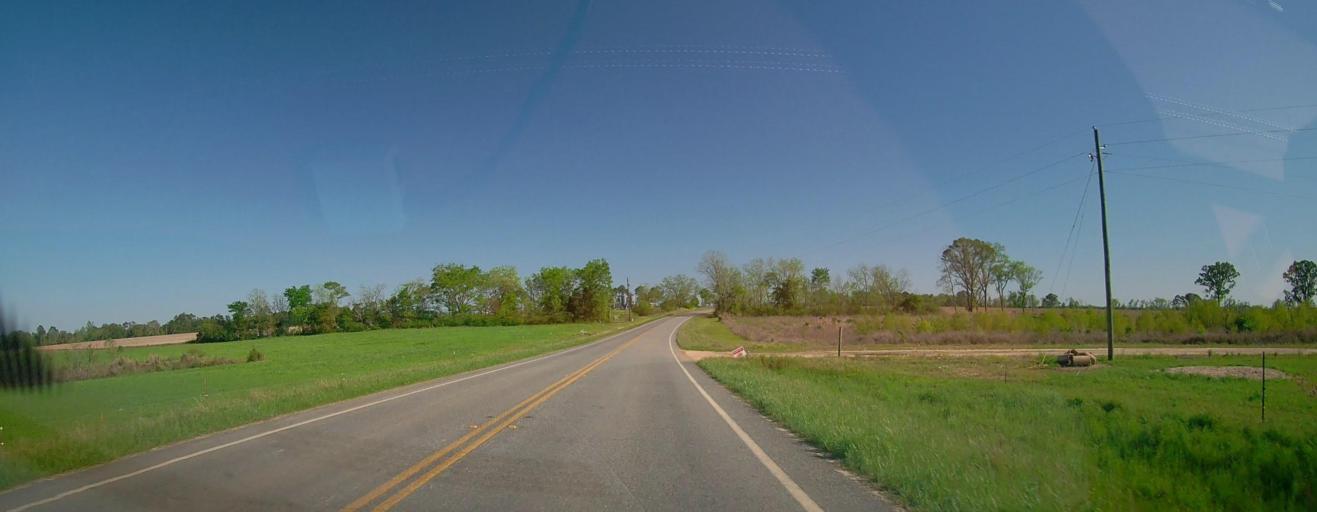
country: US
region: Georgia
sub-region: Wilcox County
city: Rochelle
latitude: 31.9824
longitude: -83.4582
